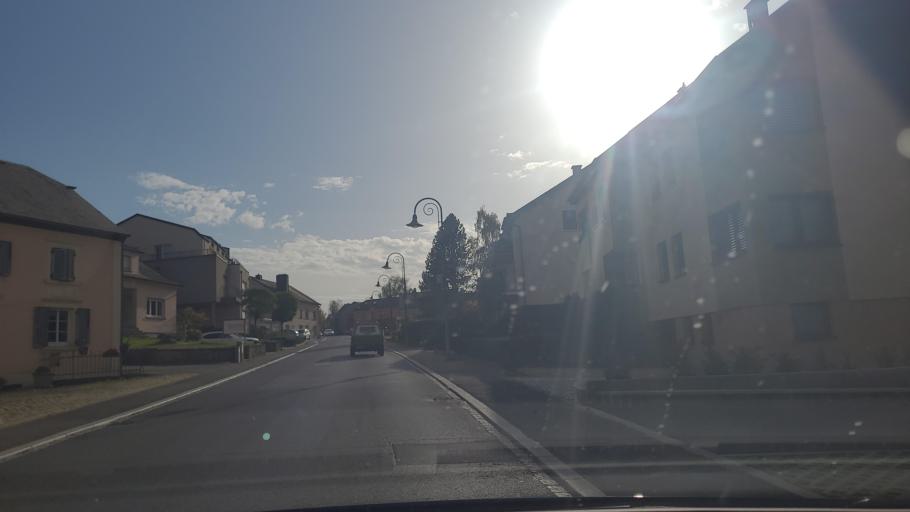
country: LU
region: Luxembourg
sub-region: Canton de Capellen
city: Kehlen
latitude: 49.6657
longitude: 6.0346
